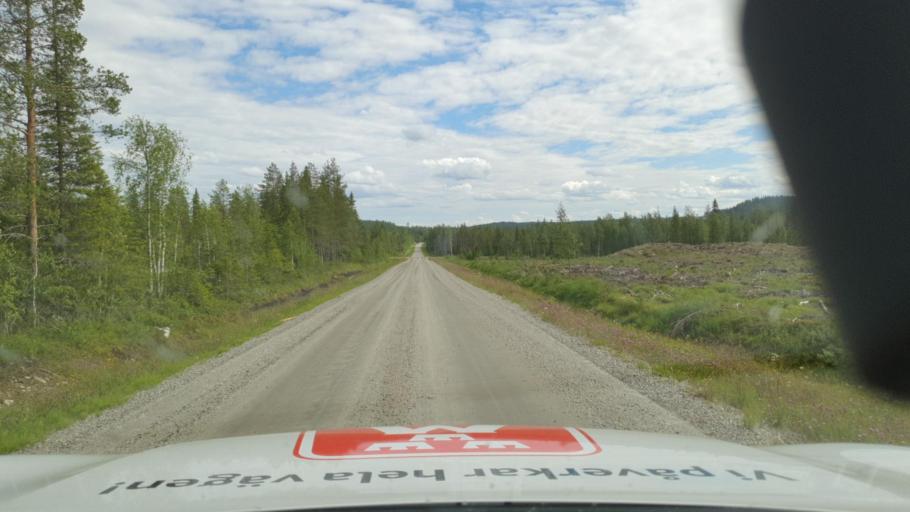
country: SE
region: Vaesterbotten
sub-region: Norsjo Kommun
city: Norsjoe
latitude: 64.8536
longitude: 19.5053
